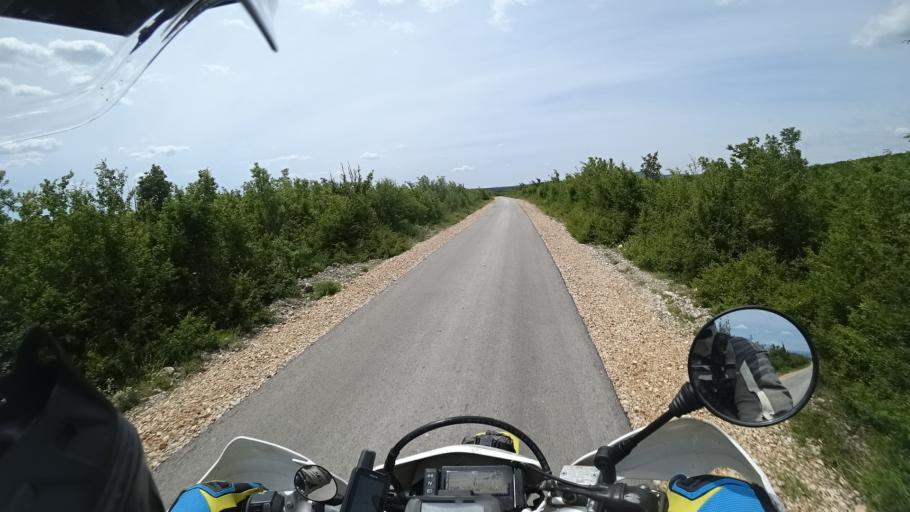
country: HR
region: Sibensko-Kniniska
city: Kistanje
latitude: 44.0726
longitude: 15.9821
